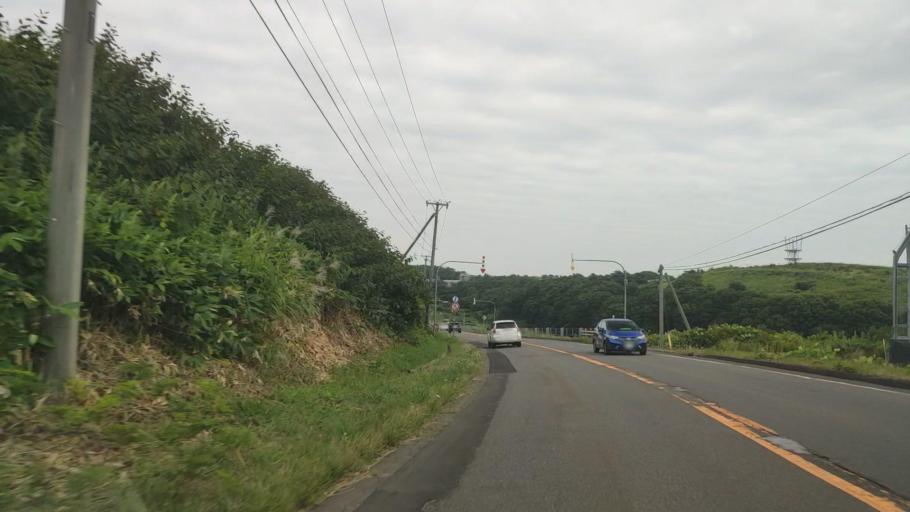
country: JP
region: Hokkaido
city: Ishikari
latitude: 43.3377
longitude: 141.4239
